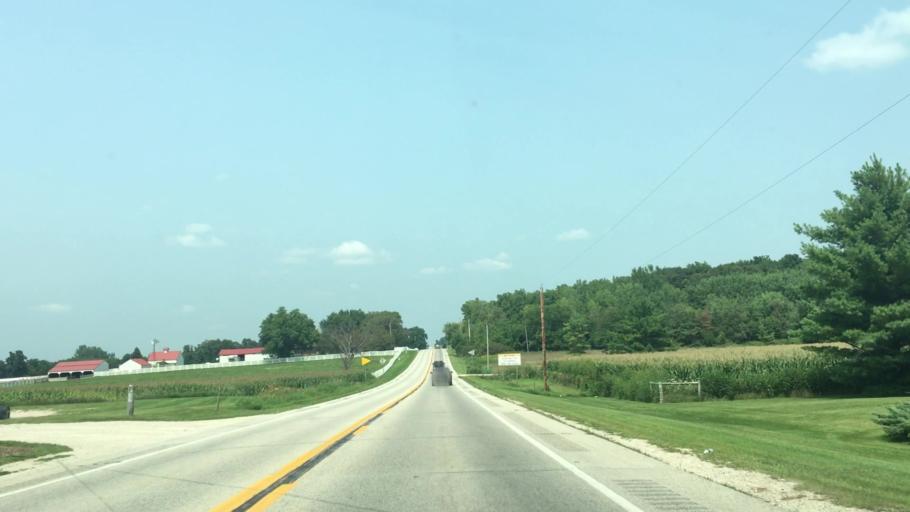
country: US
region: Iowa
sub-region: Buchanan County
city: Independence
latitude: 42.4910
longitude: -91.8895
